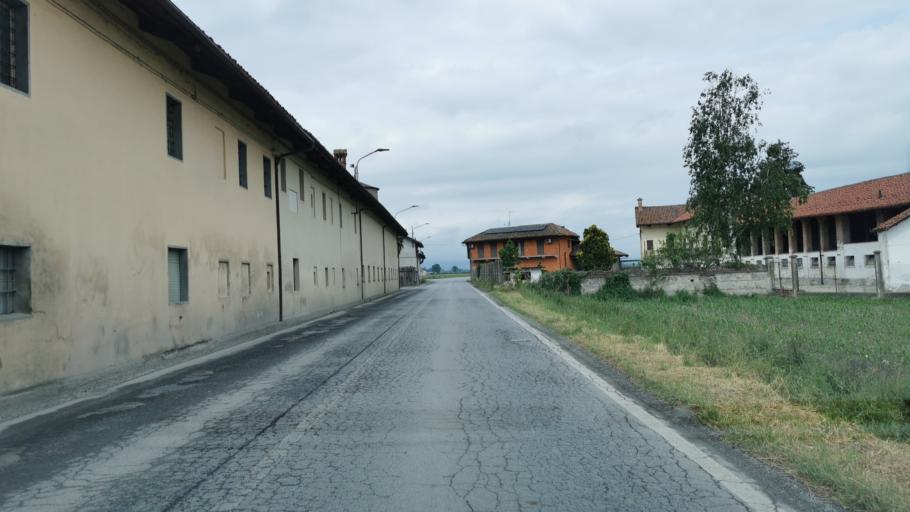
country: IT
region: Piedmont
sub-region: Provincia di Cuneo
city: Genola
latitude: 44.6102
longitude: 7.6173
